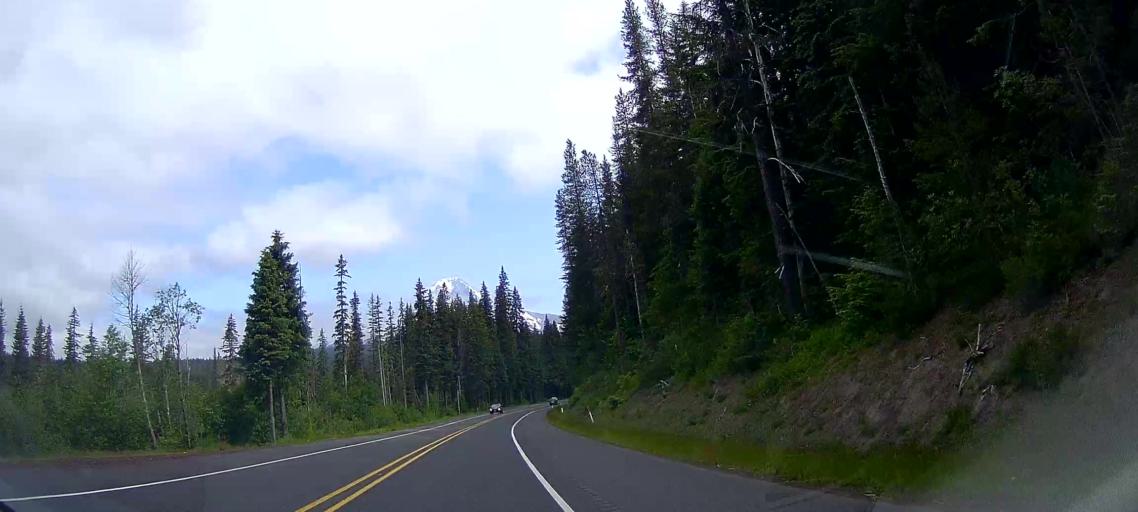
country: US
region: Oregon
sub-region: Clackamas County
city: Mount Hood Village
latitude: 45.2724
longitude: -121.7179
